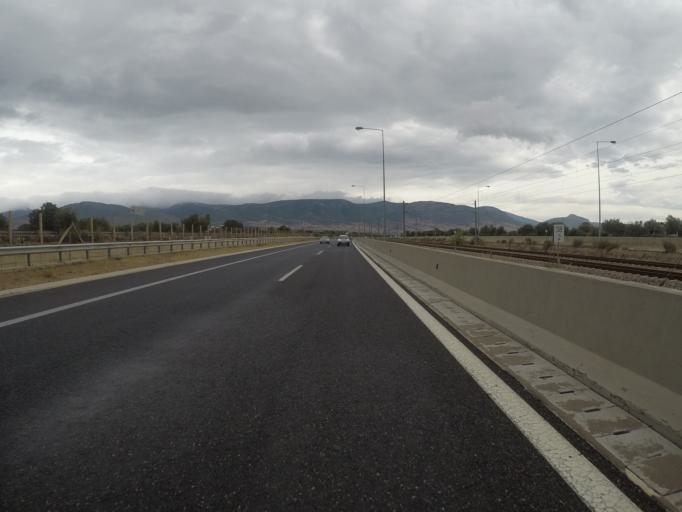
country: GR
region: Attica
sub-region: Nomarchia Dytikis Attikis
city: Magoula
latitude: 38.0855
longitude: 23.5426
